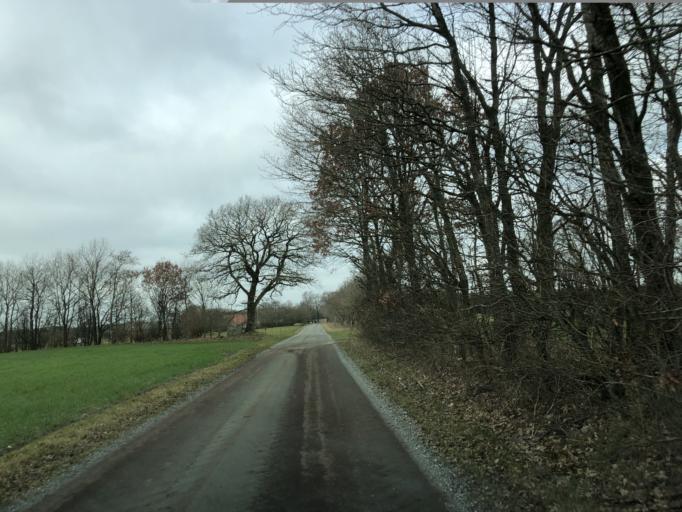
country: DK
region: South Denmark
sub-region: Billund Kommune
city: Billund
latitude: 55.7720
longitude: 9.1419
